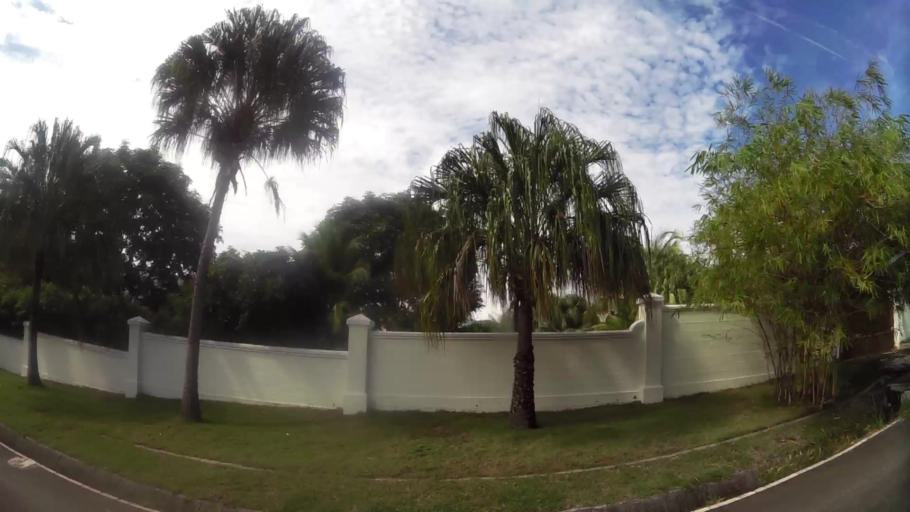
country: PA
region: Panama
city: Nueva Gorgona
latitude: 8.5464
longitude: -79.8782
